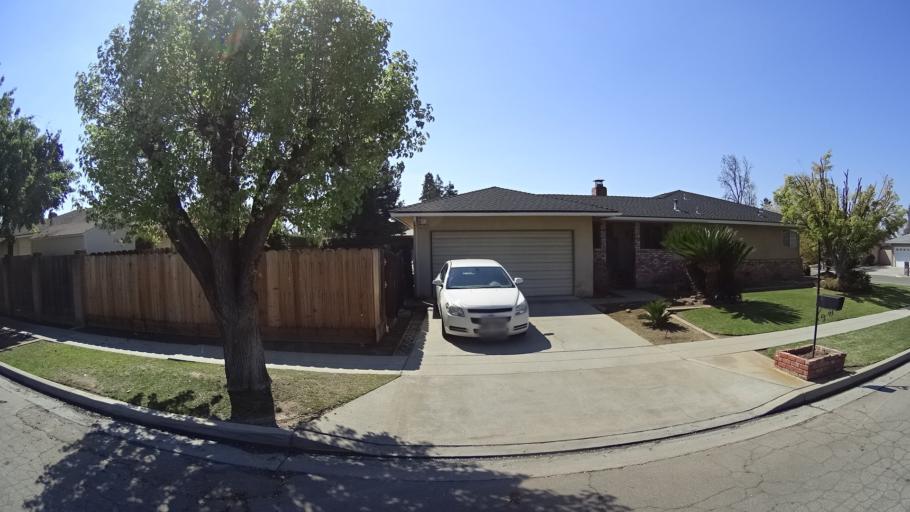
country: US
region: California
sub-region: Fresno County
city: Clovis
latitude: 36.8335
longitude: -119.7399
